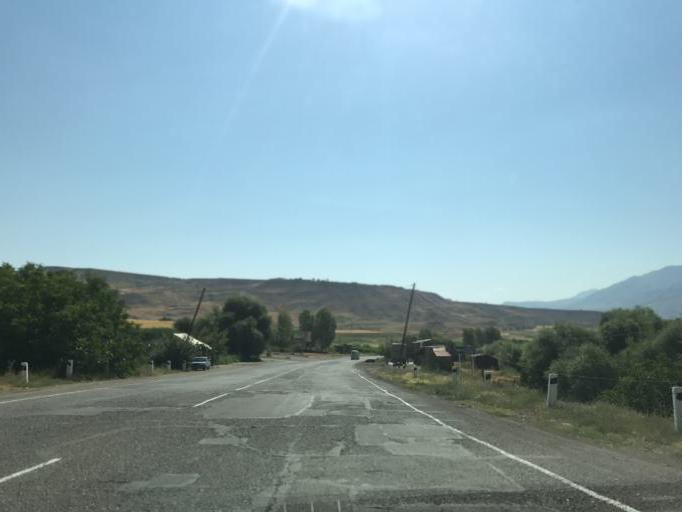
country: AM
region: Vayots' Dzori Marz
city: Rrind
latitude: 39.7616
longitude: 45.1458
